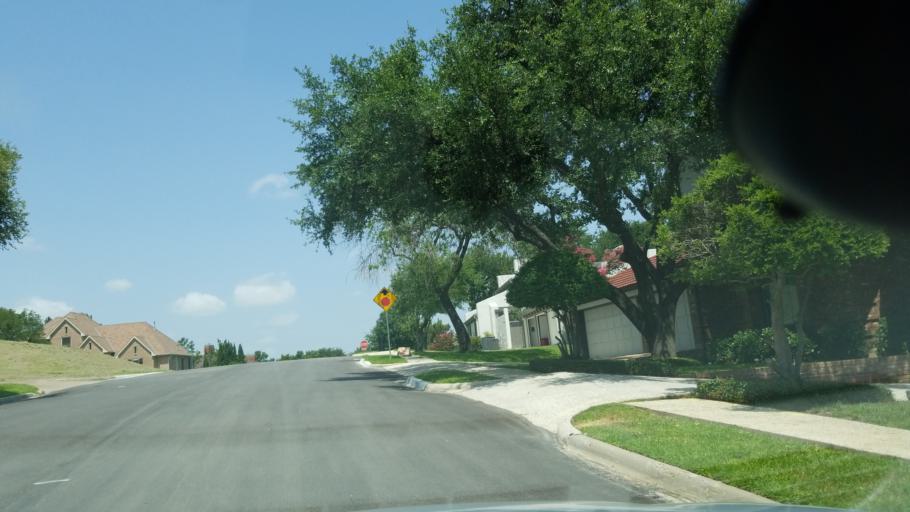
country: US
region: Texas
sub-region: Dallas County
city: Irving
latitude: 32.8537
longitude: -96.9399
